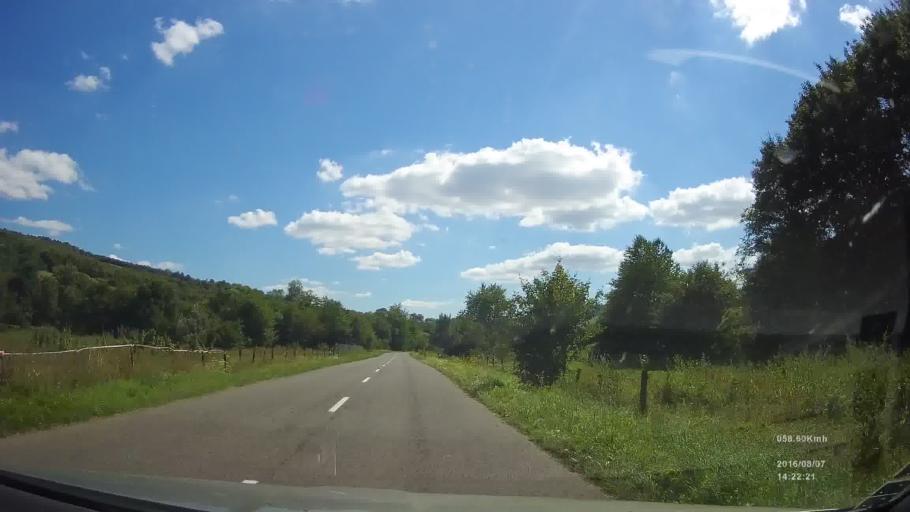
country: SK
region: Presovsky
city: Stropkov
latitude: 49.2747
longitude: 21.7517
